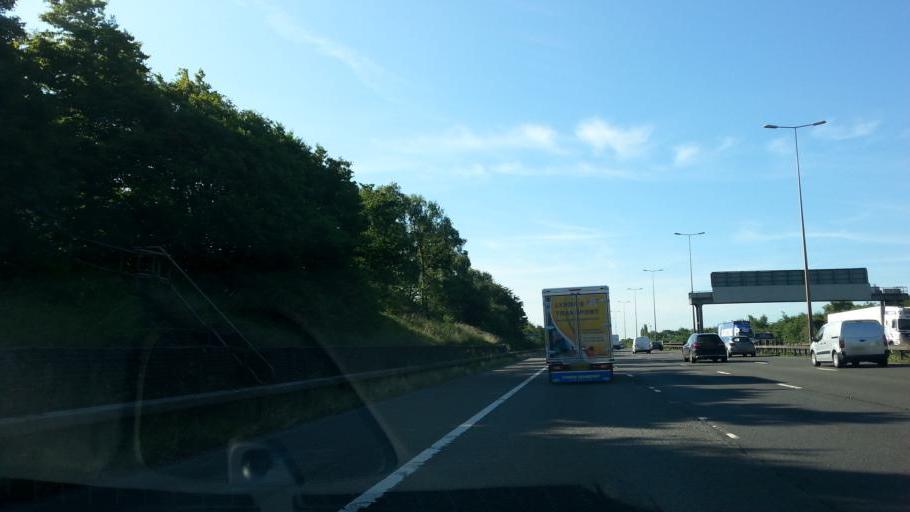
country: GB
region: England
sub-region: Leicestershire
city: Kirby Muxloe
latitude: 52.6320
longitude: -1.2148
